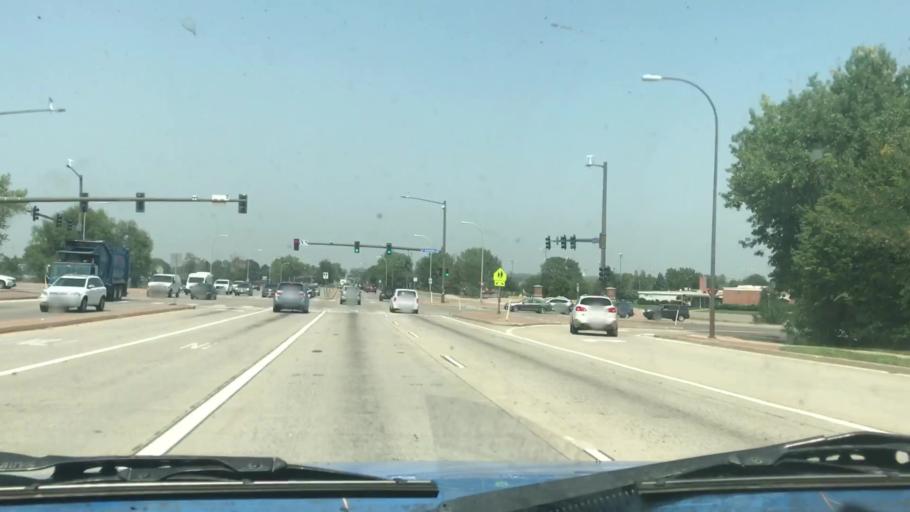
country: US
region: Colorado
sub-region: Jefferson County
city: Lakewood
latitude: 39.7104
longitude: -105.1096
